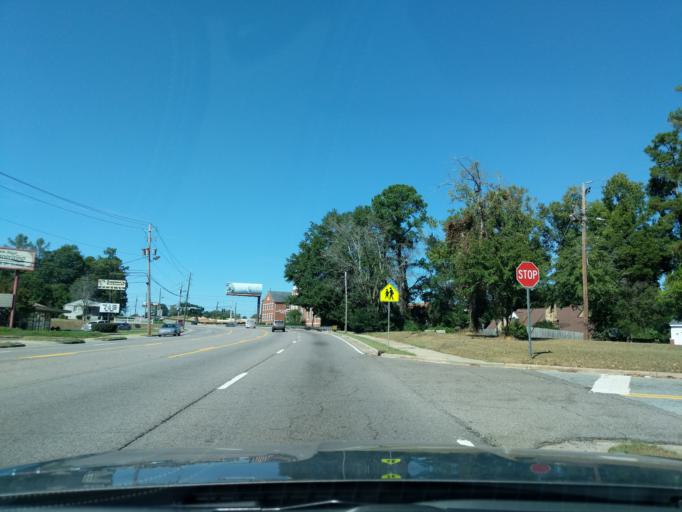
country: US
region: Georgia
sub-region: Richmond County
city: Augusta
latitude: 33.4980
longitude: -82.0112
